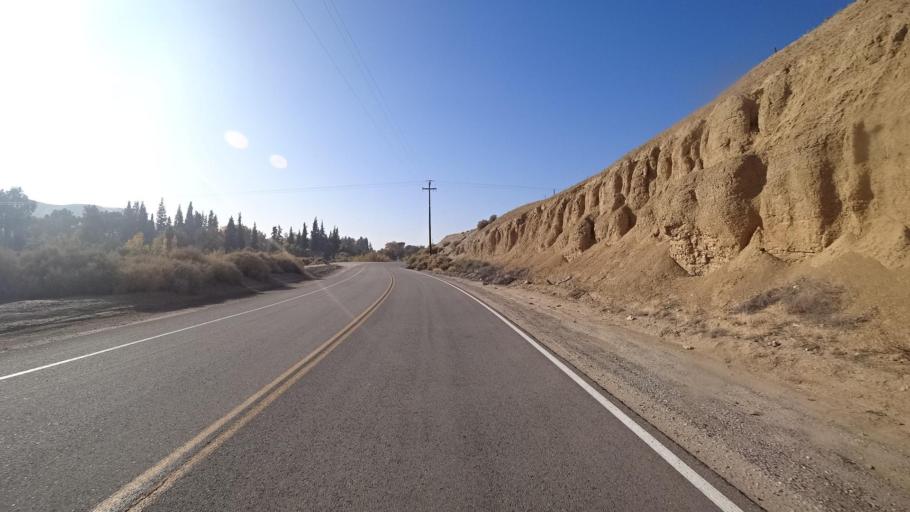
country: US
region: California
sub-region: Kern County
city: Oildale
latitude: 35.4510
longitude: -118.9036
